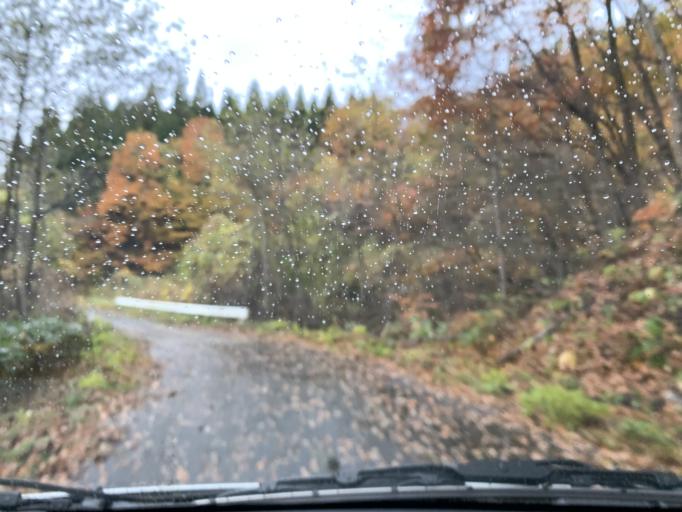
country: JP
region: Iwate
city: Mizusawa
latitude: 39.1033
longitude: 140.9444
